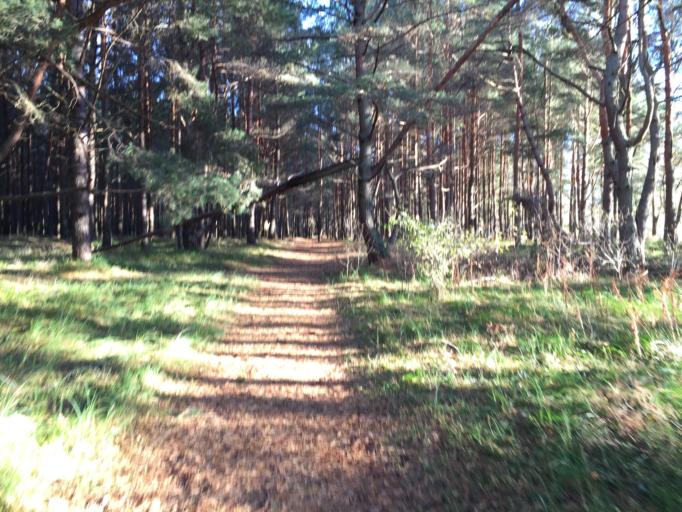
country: LV
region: Carnikava
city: Carnikava
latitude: 57.1557
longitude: 24.2750
